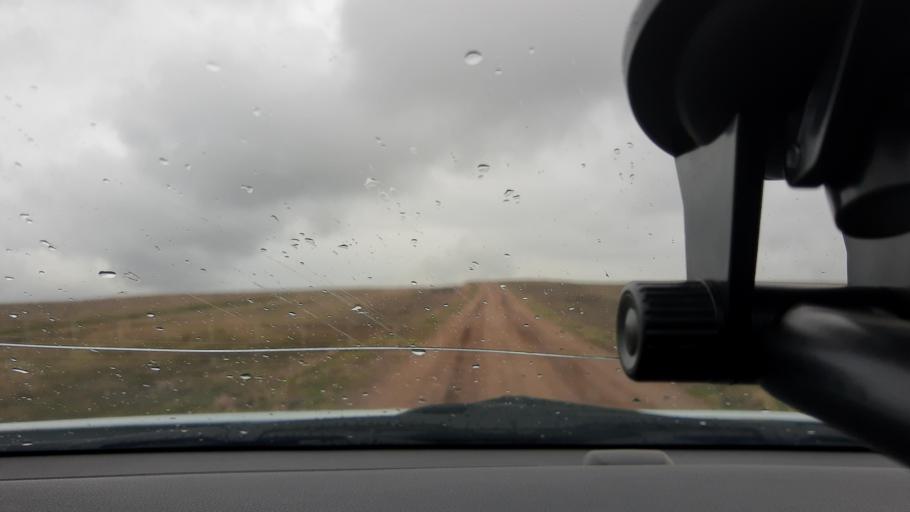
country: RU
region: Bashkortostan
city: Pavlovka
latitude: 55.4329
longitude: 56.3165
